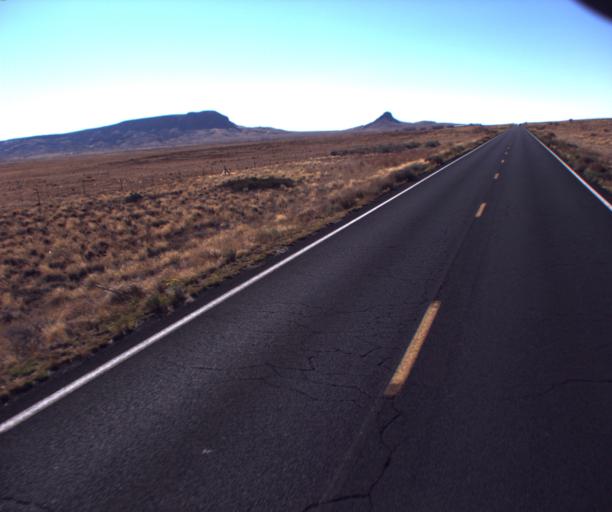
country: US
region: Arizona
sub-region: Navajo County
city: Dilkon
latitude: 35.4574
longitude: -110.4228
